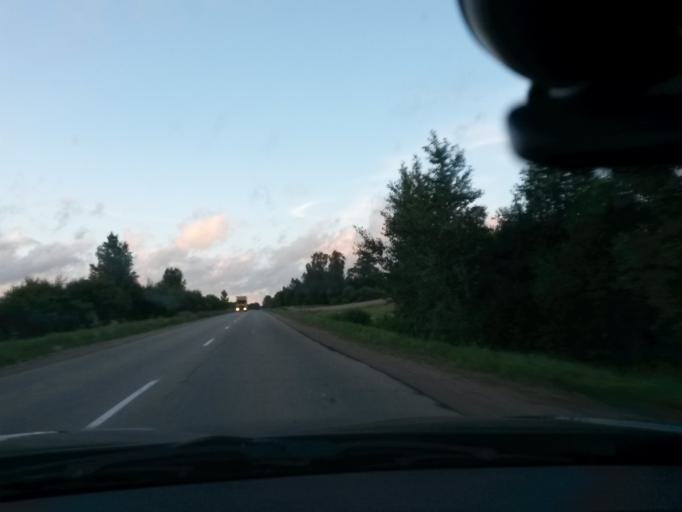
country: LV
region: Madonas Rajons
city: Madona
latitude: 56.7307
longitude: 26.0086
